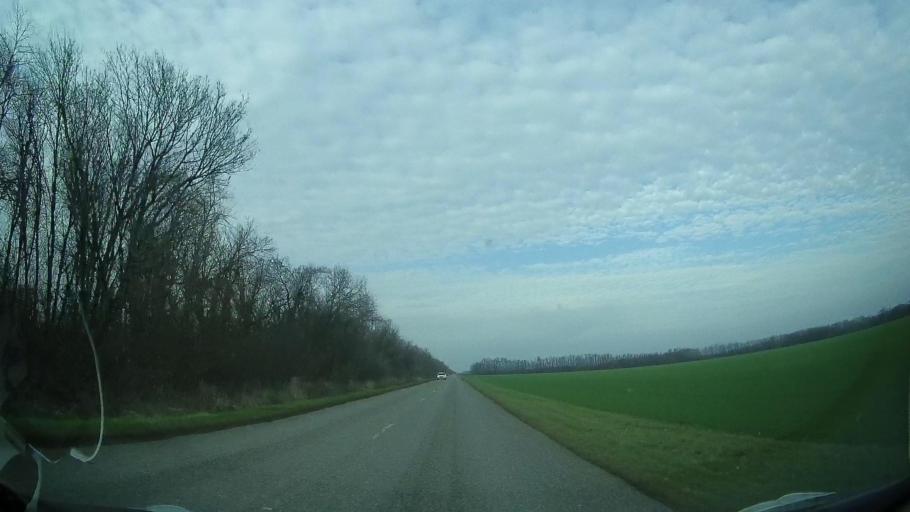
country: RU
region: Rostov
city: Zernograd
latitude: 46.9826
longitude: 40.3916
